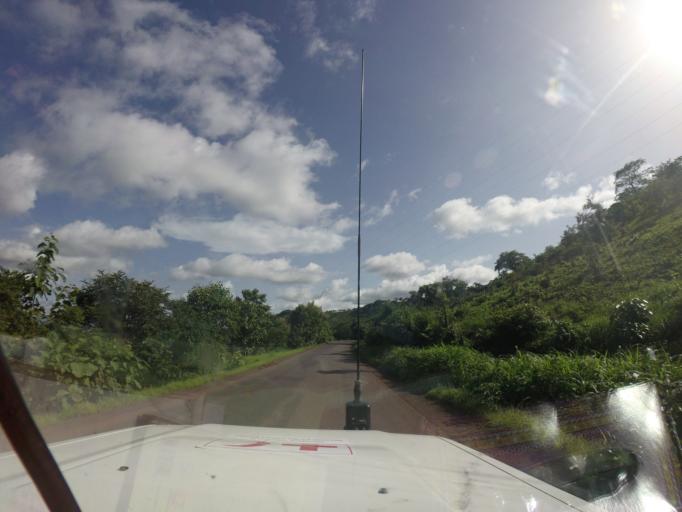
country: GN
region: Mamou
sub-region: Mamou Prefecture
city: Mamou
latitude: 10.2456
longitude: -12.4575
